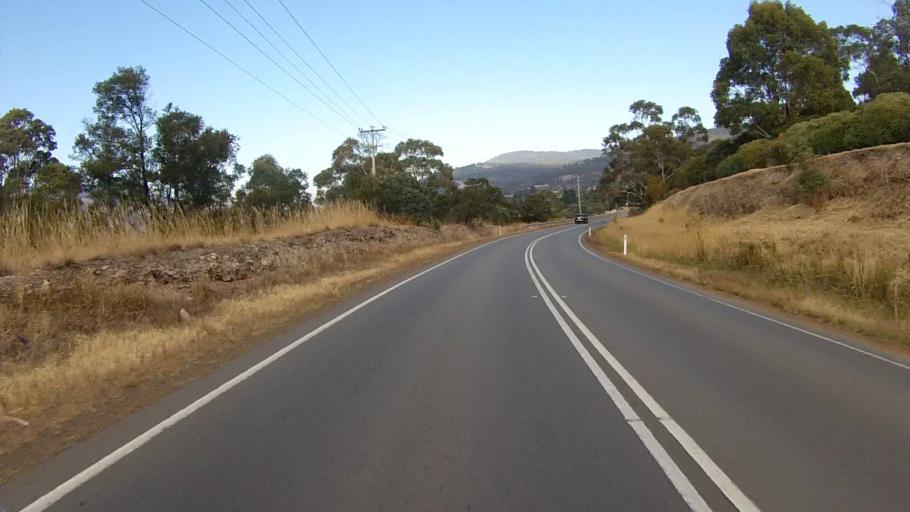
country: AU
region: Tasmania
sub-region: Brighton
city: Bridgewater
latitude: -42.7263
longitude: 147.1938
